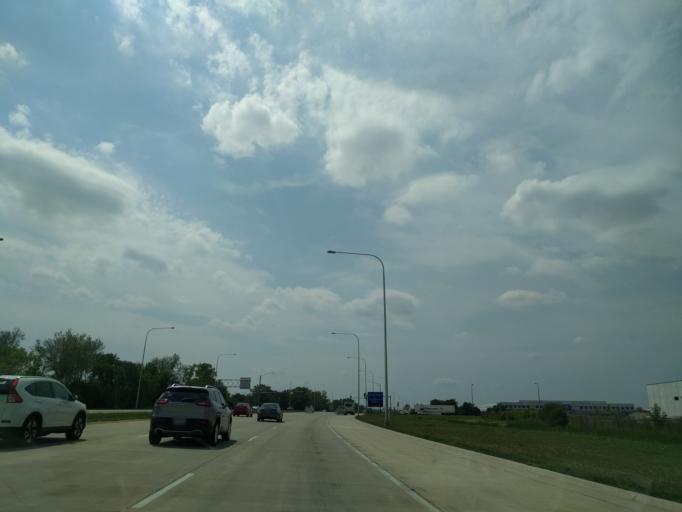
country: US
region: Illinois
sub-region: Cook County
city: Schiller Park
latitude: 41.9633
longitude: -87.8781
